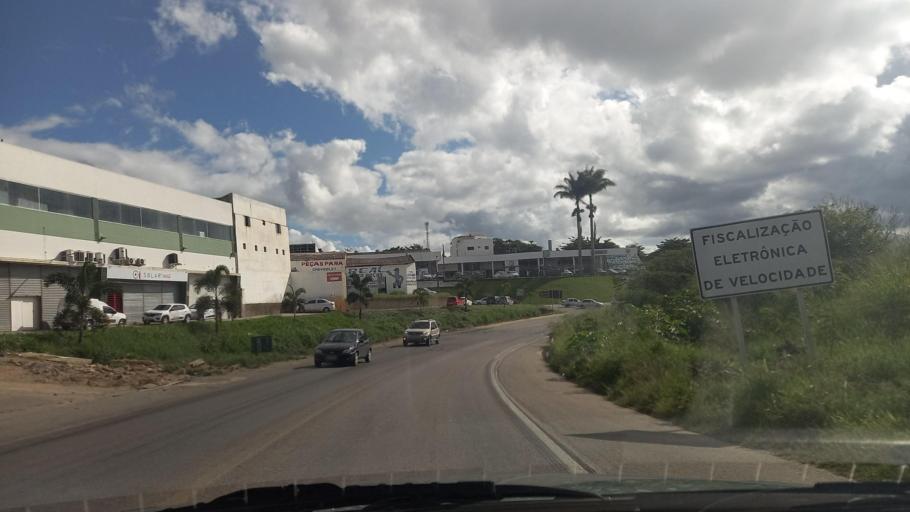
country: BR
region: Pernambuco
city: Garanhuns
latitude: -8.8793
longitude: -36.4787
